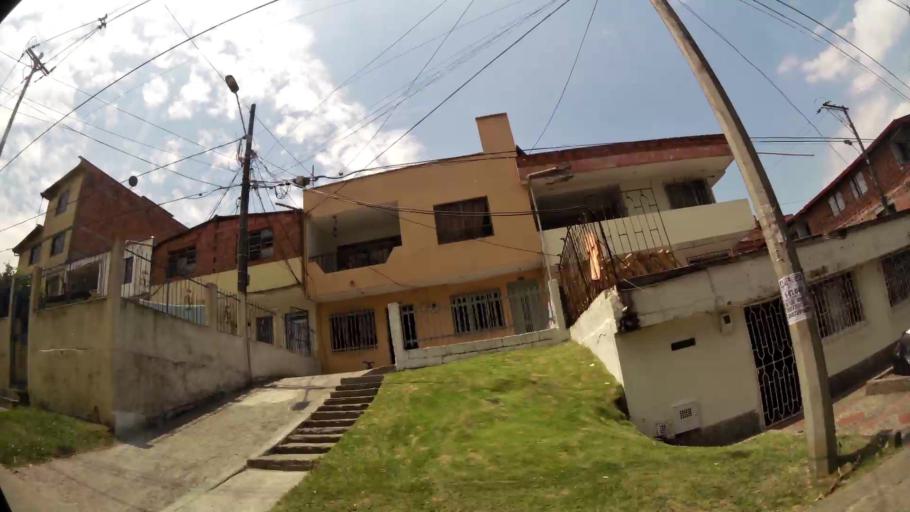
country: CO
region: Antioquia
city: Bello
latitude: 6.3071
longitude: -75.5669
